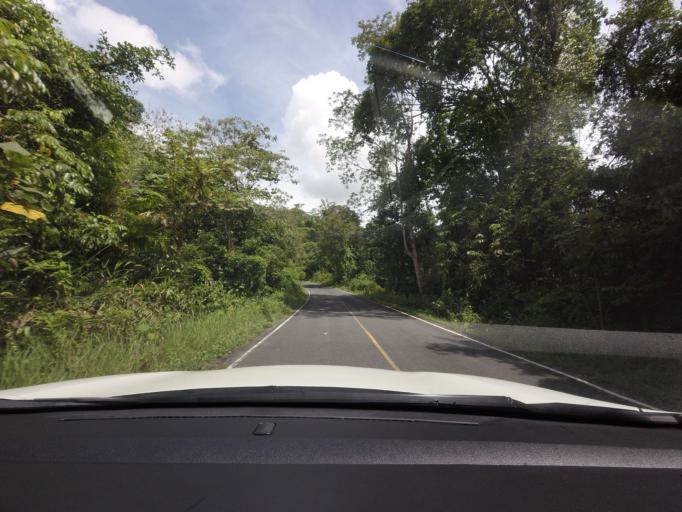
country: TH
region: Nakhon Nayok
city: Pak Phli
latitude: 14.2977
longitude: 101.3923
